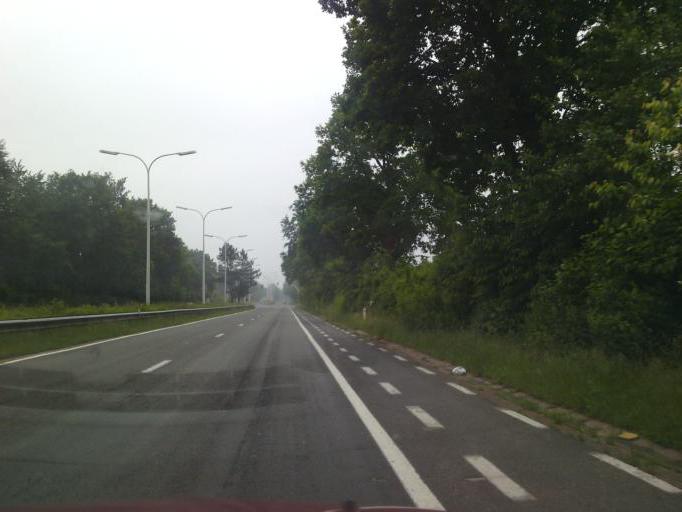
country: BE
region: Flanders
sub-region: Provincie Oost-Vlaanderen
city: Aalst
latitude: 50.9669
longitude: 4.0393
